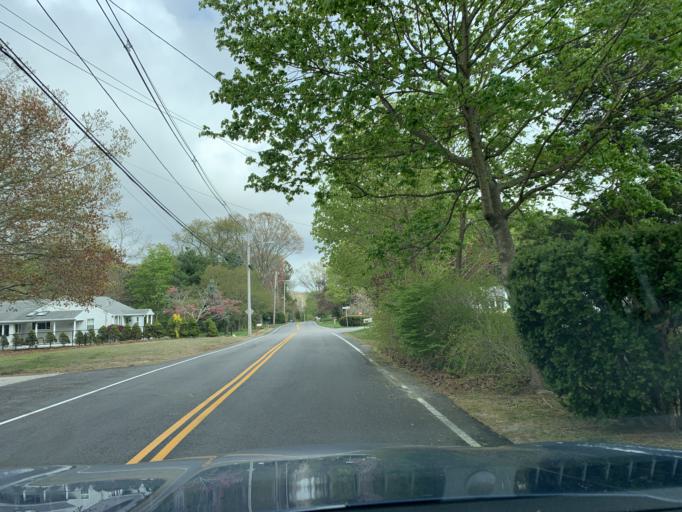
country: US
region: Rhode Island
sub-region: Washington County
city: North Kingstown
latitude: 41.6037
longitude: -71.4843
